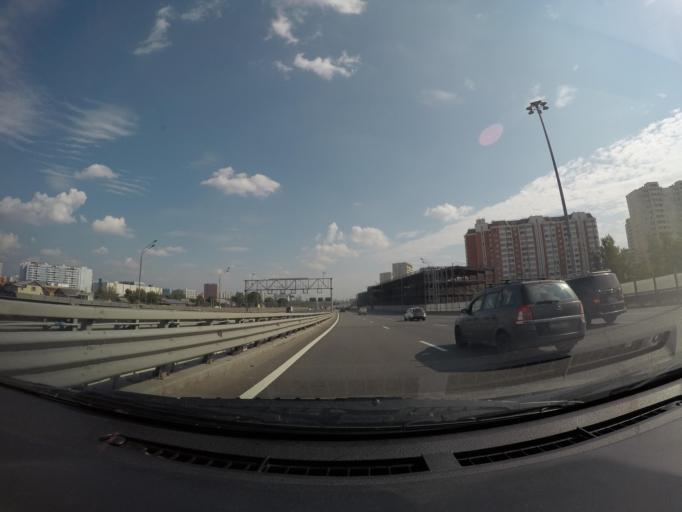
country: RU
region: Moskovskaya
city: Levoberezhnaya
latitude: 55.8790
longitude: 37.4864
